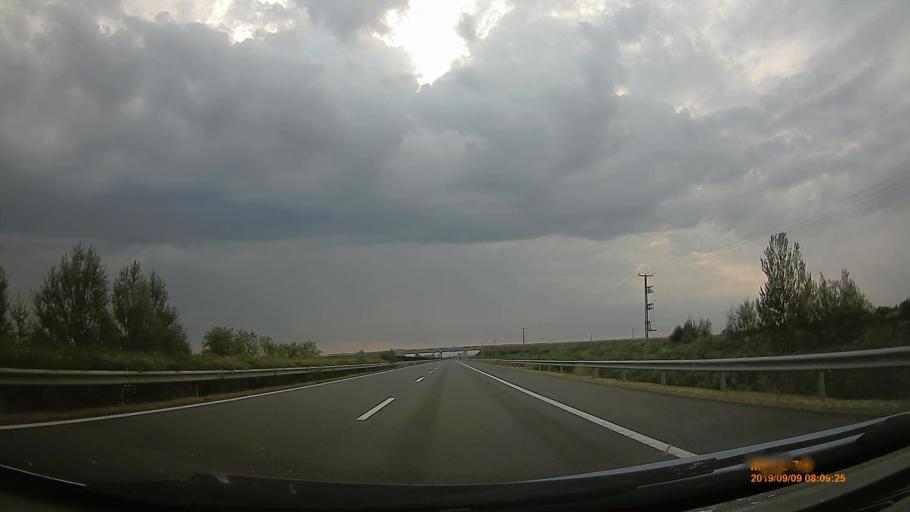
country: HU
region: Hajdu-Bihar
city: Gorbehaza
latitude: 47.7981
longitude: 21.2257
